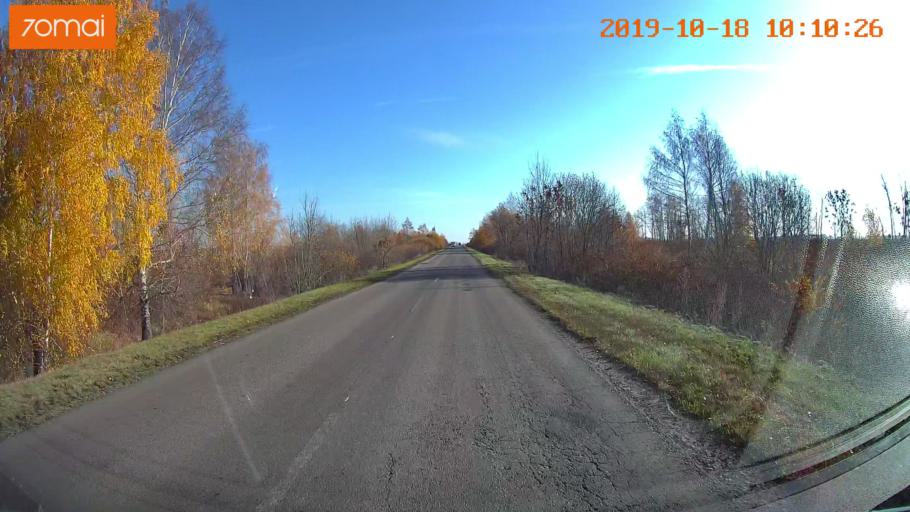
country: RU
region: Tula
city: Kurkino
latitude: 53.3790
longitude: 38.4761
